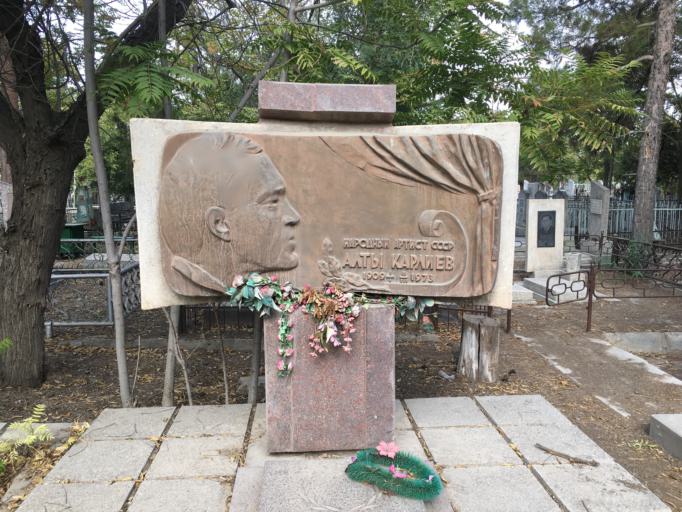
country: TM
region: Ahal
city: Ashgabat
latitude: 37.9709
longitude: 58.3558
